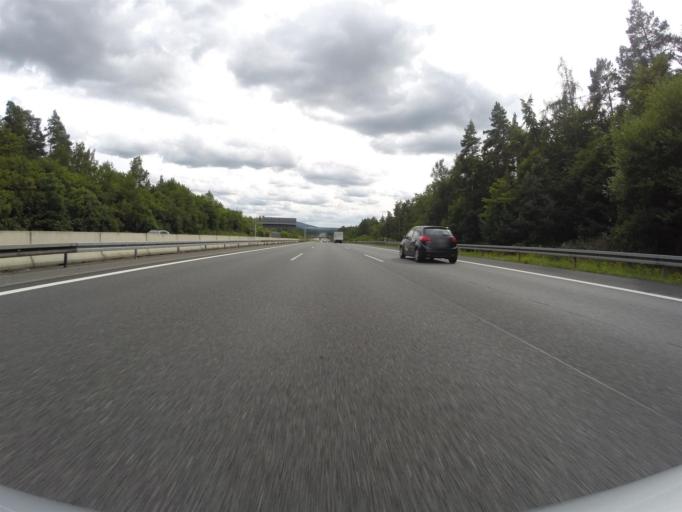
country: DE
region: Bavaria
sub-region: Regierungsbezirk Mittelfranken
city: Schnaittach
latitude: 49.5568
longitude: 11.3241
